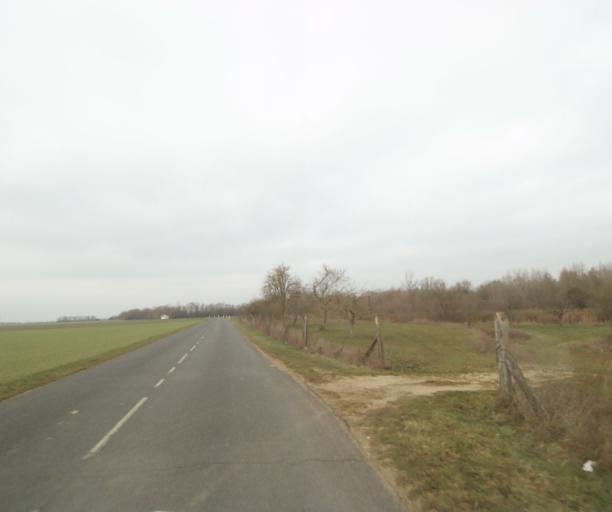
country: FR
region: Champagne-Ardenne
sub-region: Departement de la Haute-Marne
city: Villiers-en-Lieu
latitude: 48.6529
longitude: 4.7999
